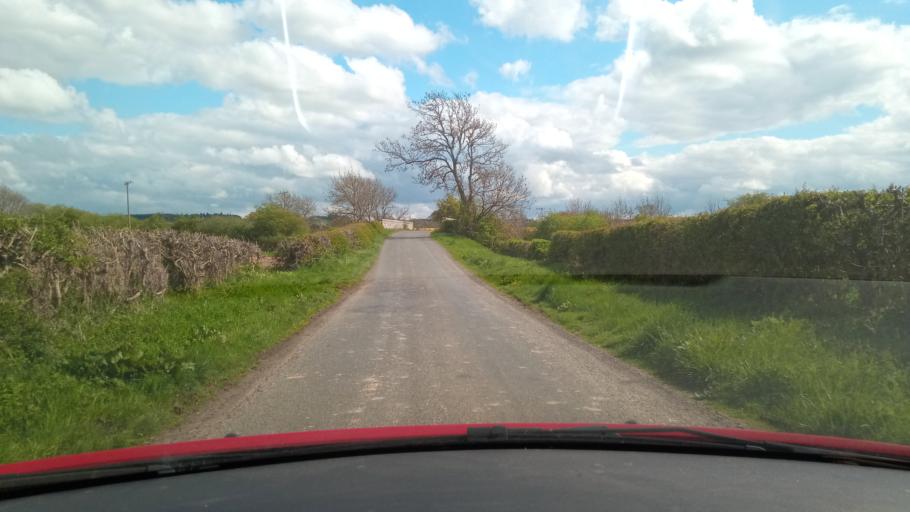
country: GB
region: Scotland
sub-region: The Scottish Borders
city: Saint Boswells
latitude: 55.5616
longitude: -2.6173
